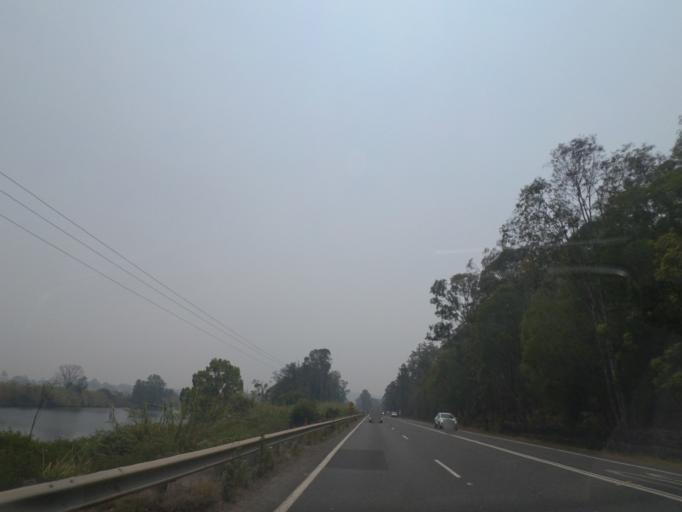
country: AU
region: New South Wales
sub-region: Clarence Valley
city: Maclean
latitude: -29.5578
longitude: 153.1506
